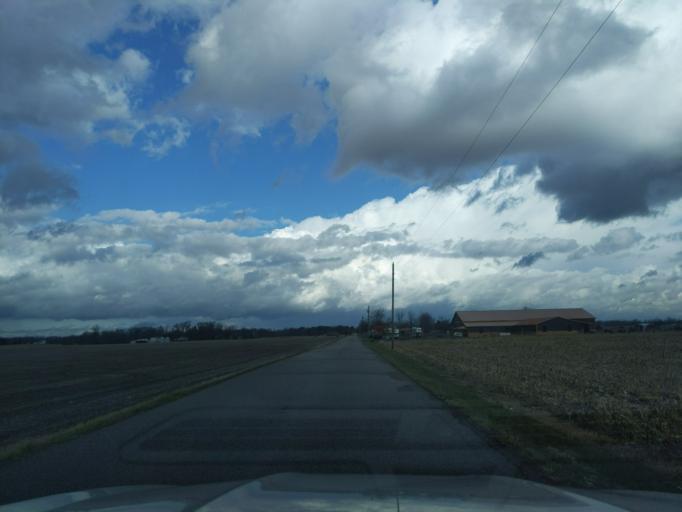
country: US
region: Indiana
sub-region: Decatur County
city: Saint Paul
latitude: 39.3952
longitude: -85.5599
